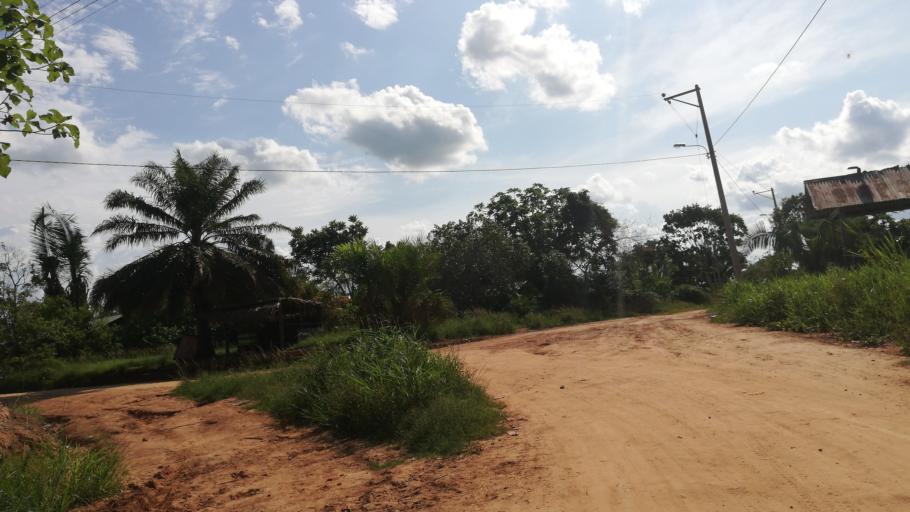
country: PE
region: Ucayali
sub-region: Provincia de Coronel Portillo
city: Puerto Callao
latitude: -8.2695
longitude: -74.6481
